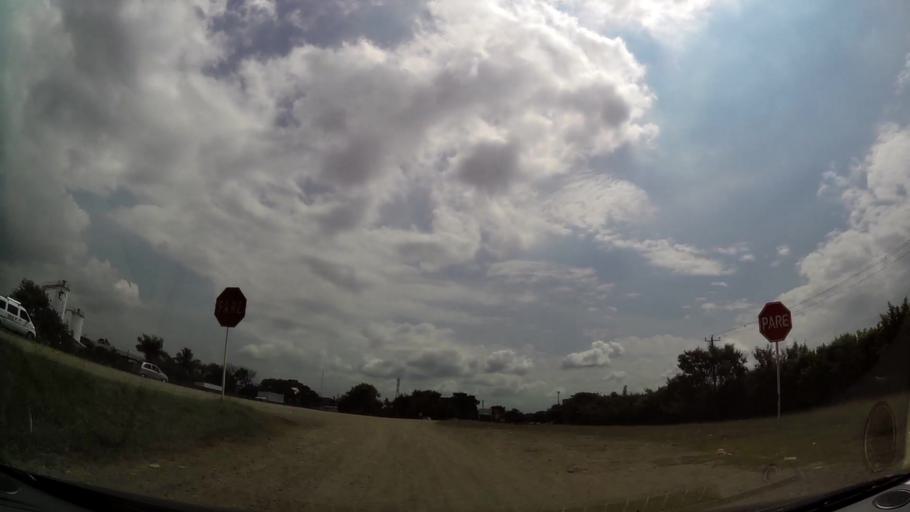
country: CO
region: Valle del Cauca
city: Cali
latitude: 3.4928
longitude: -76.4807
